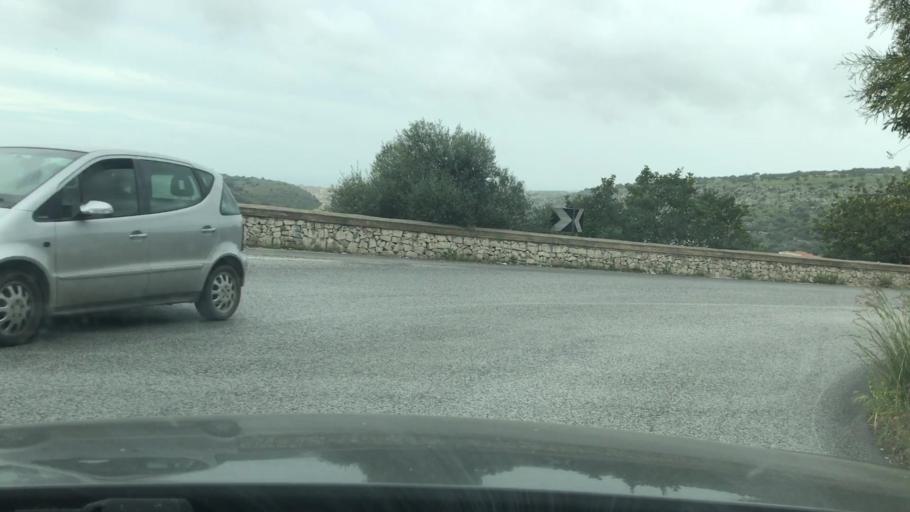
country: IT
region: Sicily
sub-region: Ragusa
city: Scicli
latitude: 36.7953
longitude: 14.7107
